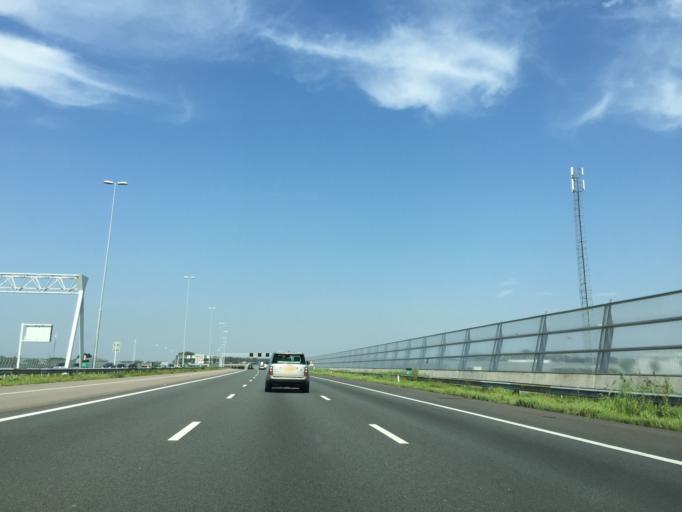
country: NL
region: South Holland
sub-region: Gemeente Kaag en Braassem
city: Oude Wetering
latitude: 52.2091
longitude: 4.6231
